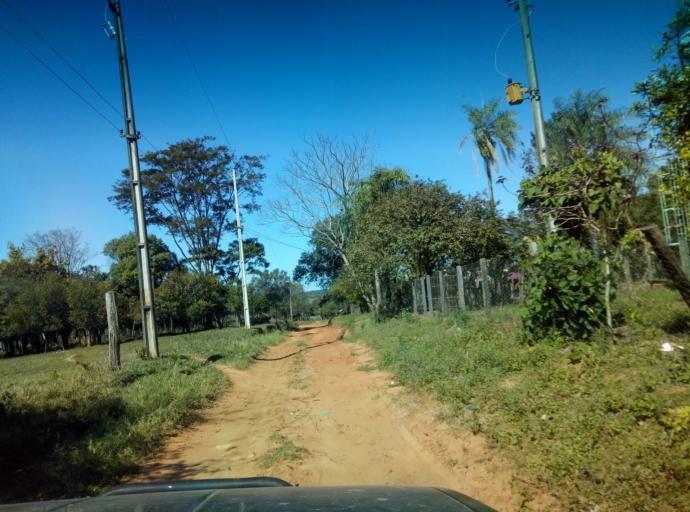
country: PY
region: Caaguazu
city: Doctor Cecilio Baez
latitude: -25.1782
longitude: -56.2020
